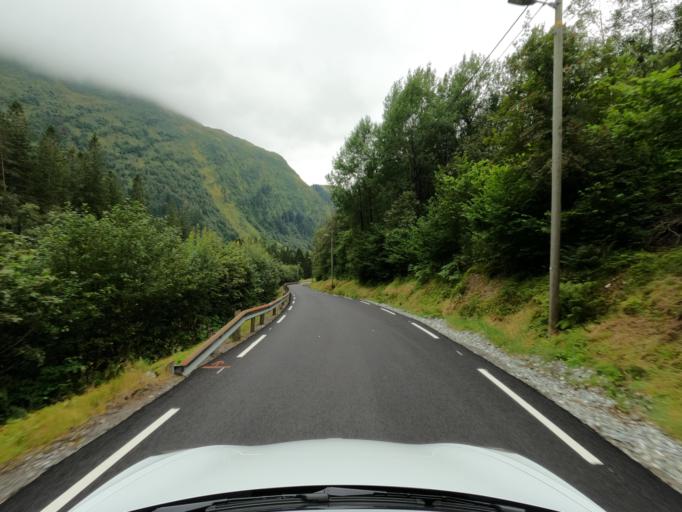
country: NO
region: Hordaland
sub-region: Bergen
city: Espeland
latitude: 60.3703
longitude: 5.4929
